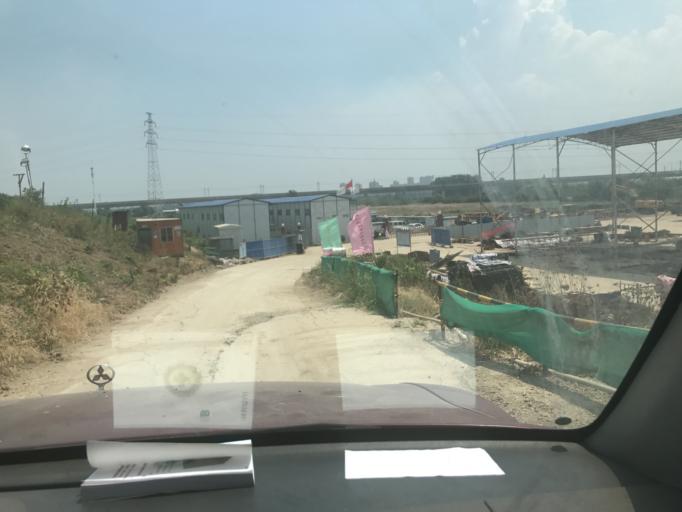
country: CN
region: Hubei
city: Zhanjiaji
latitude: 30.6846
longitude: 114.3400
